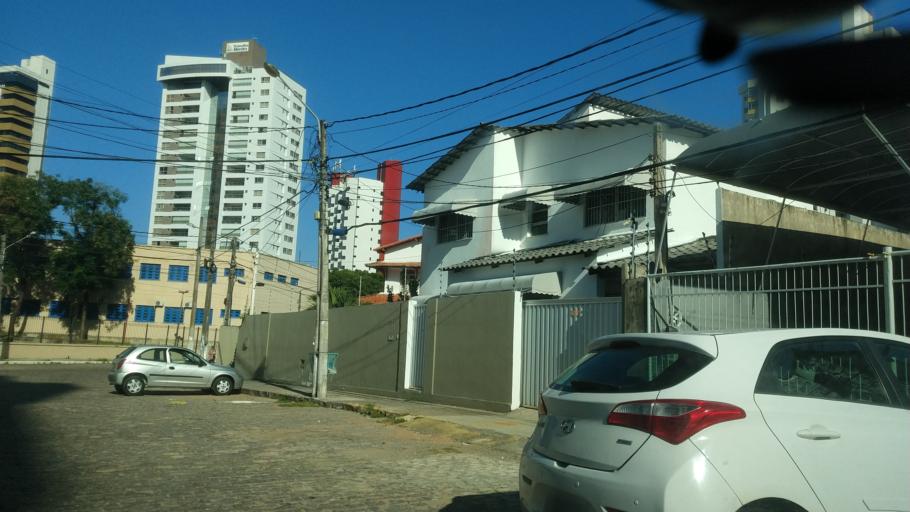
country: BR
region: Rio Grande do Norte
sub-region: Natal
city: Natal
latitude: -5.7839
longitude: -35.1974
